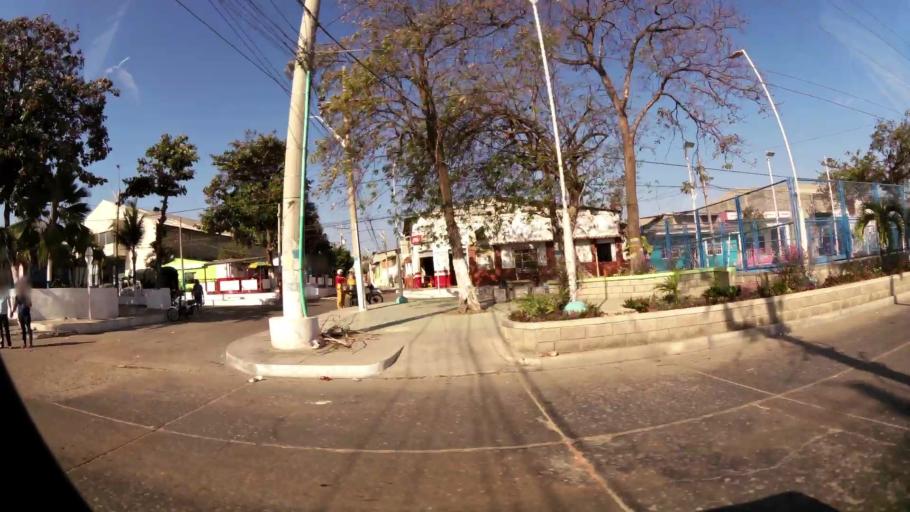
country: CO
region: Atlantico
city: Barranquilla
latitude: 10.9929
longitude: -74.7832
